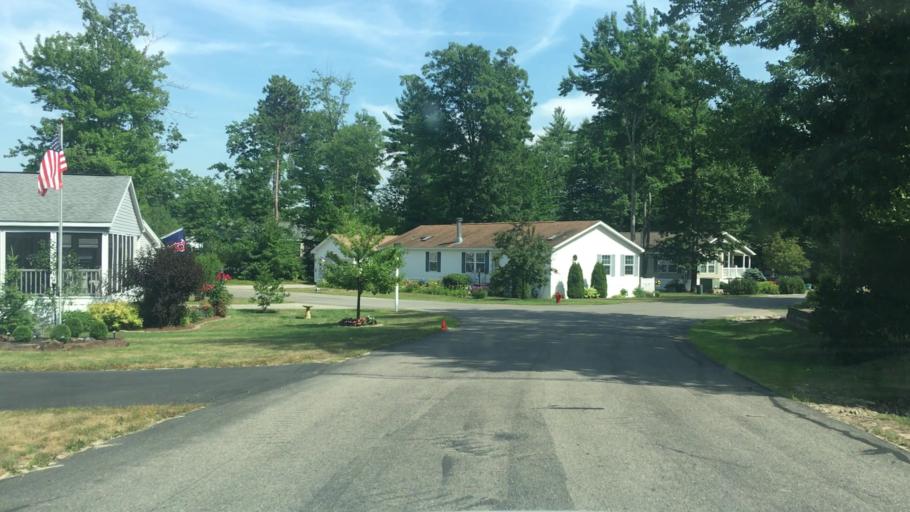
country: US
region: New Hampshire
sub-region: Strafford County
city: Rochester
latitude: 43.3157
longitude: -70.9241
